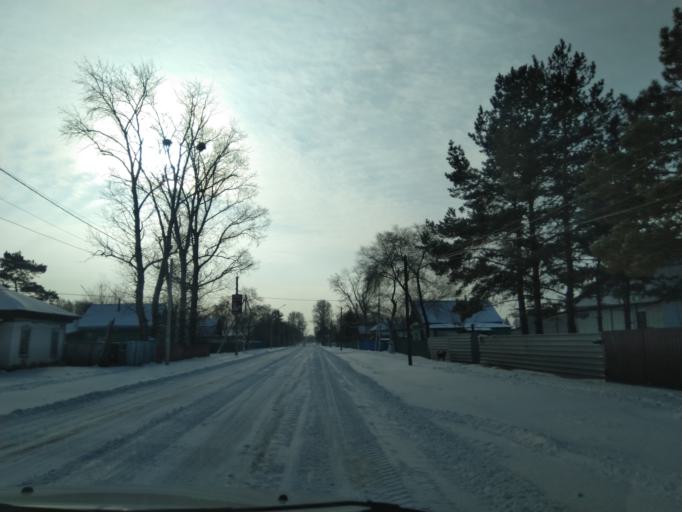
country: RU
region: Amur
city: Poyarkovo
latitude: 49.6279
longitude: 128.6499
